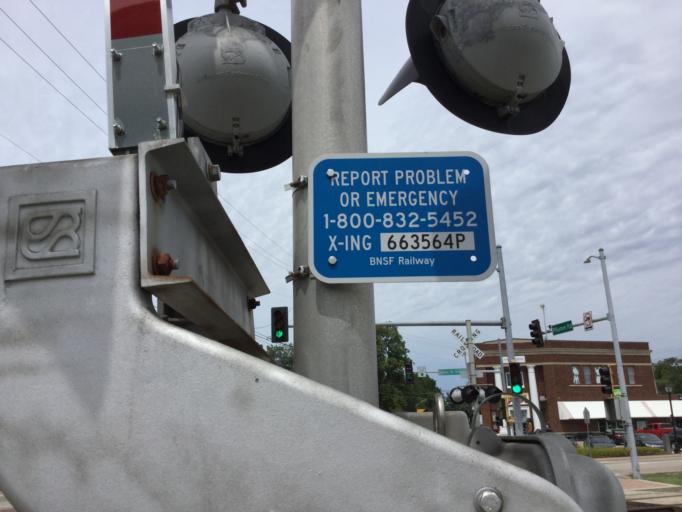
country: US
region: Kansas
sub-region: Johnson County
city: Lenexa
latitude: 38.9600
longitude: -94.7422
